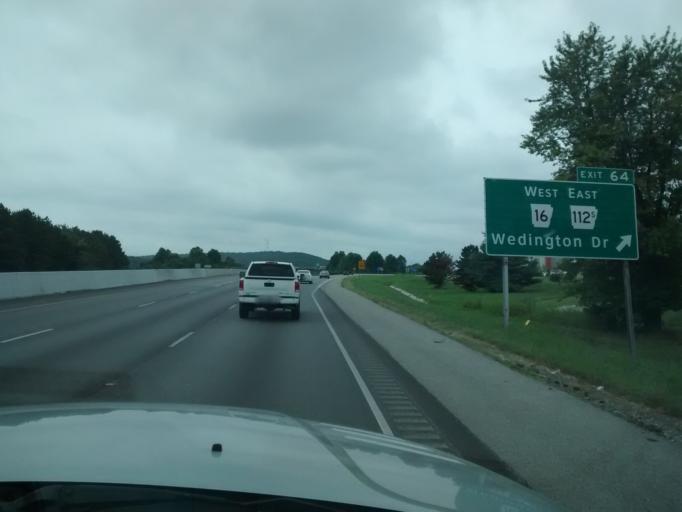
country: US
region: Arkansas
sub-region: Washington County
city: Fayetteville
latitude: 36.0825
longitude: -94.1987
